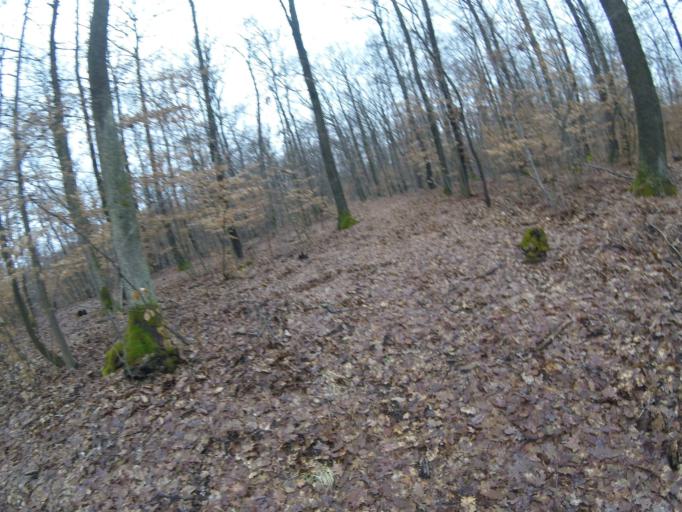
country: HU
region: Borsod-Abauj-Zemplen
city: Rudabanya
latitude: 48.4500
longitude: 20.5755
